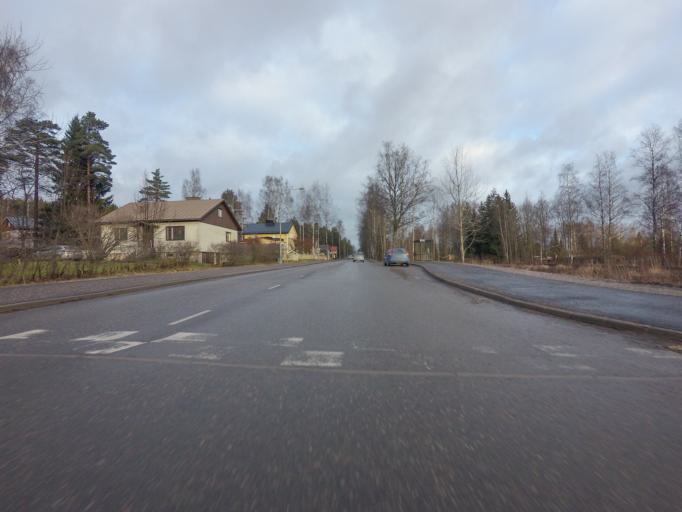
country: FI
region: Uusimaa
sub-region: Helsinki
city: Lohja
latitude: 60.2502
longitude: 24.0929
